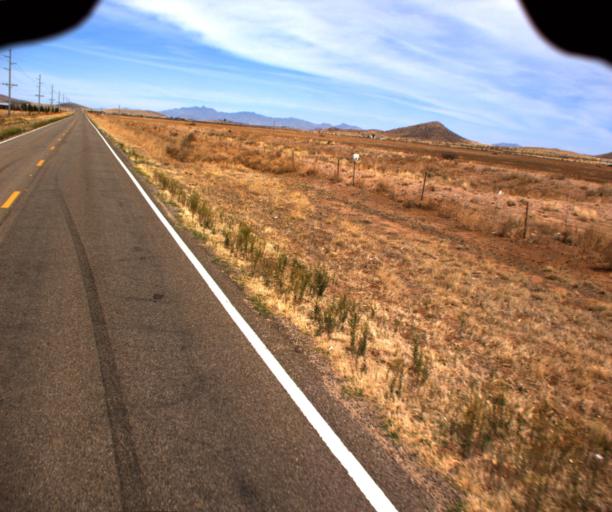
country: US
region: Arizona
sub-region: Cochise County
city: Tombstone
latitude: 31.8426
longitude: -109.6952
